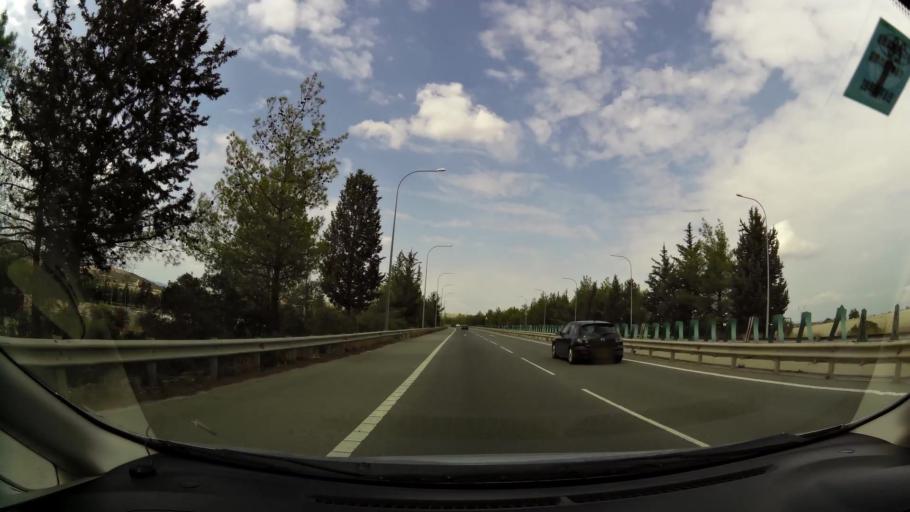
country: CY
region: Lefkosia
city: Alampra
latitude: 35.0028
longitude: 33.3955
